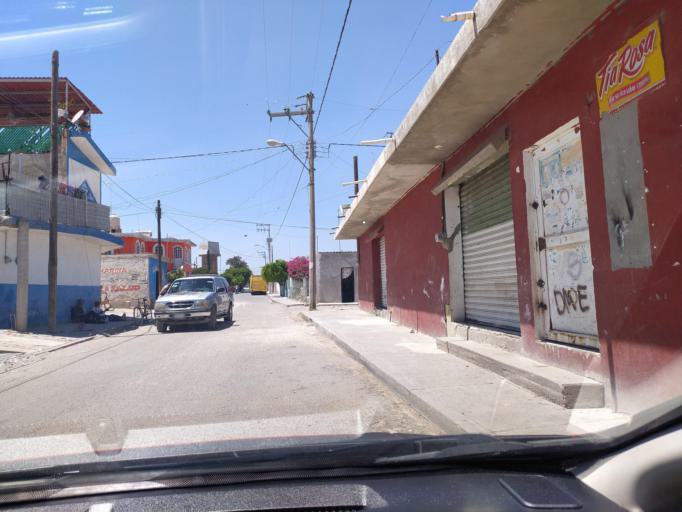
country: MX
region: Guanajuato
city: San Roque
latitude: 20.9466
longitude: -101.8567
